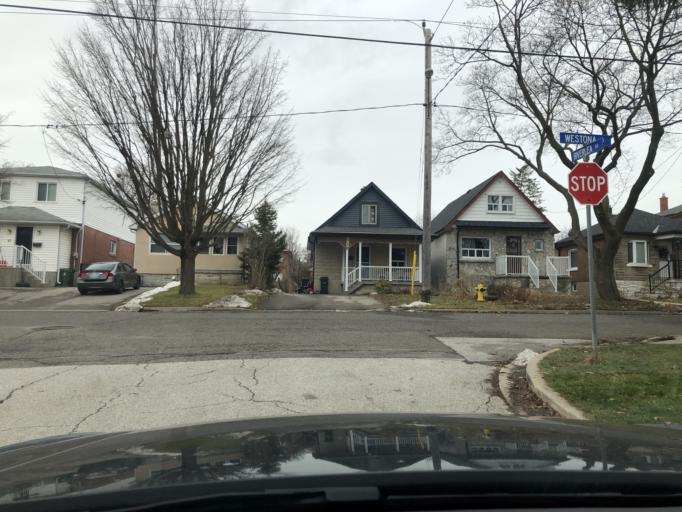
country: CA
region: Ontario
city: Etobicoke
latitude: 43.6982
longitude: -79.5275
